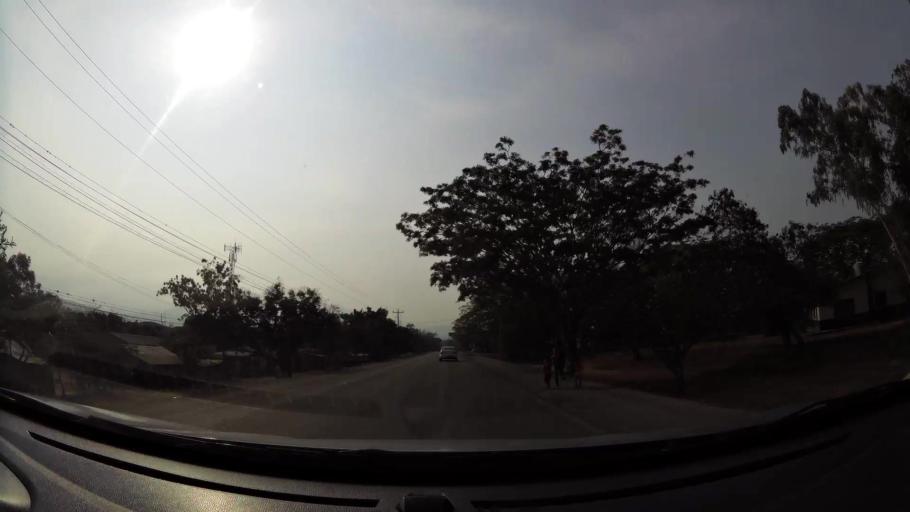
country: HN
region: Comayagua
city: Comayagua
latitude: 14.4567
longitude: -87.6566
